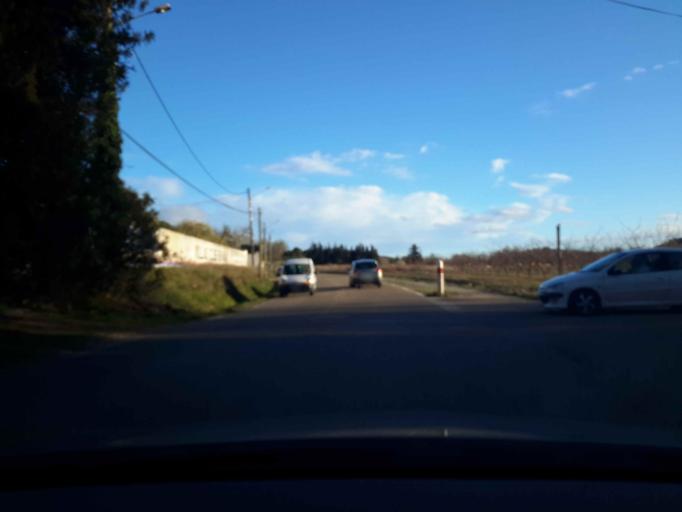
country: FR
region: Languedoc-Roussillon
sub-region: Departement du Gard
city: Generac
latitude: 43.7386
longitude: 4.3435
